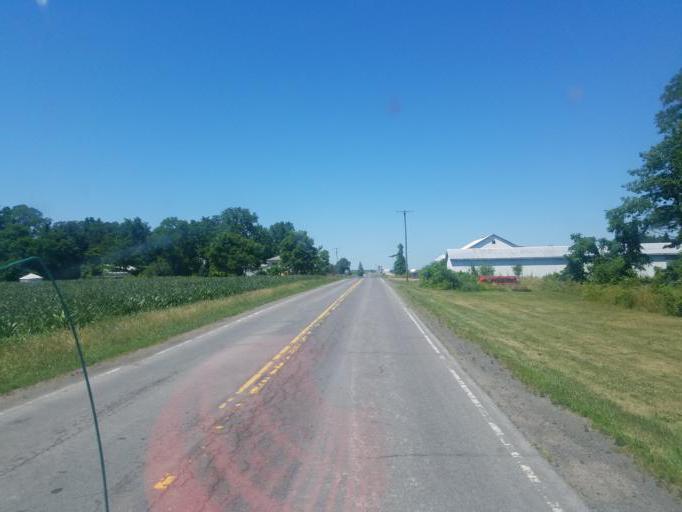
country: US
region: New York
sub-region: Yates County
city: Penn Yan
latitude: 42.7224
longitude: -76.9978
